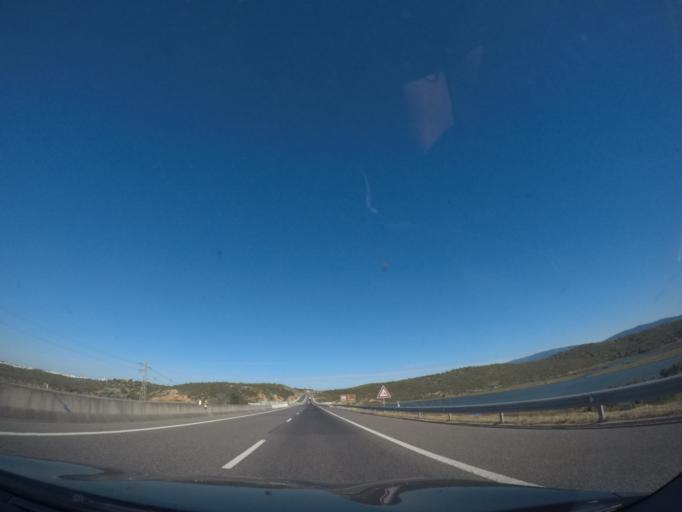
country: PT
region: Faro
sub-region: Lagoa
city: Estombar
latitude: 37.1606
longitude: -8.4994
